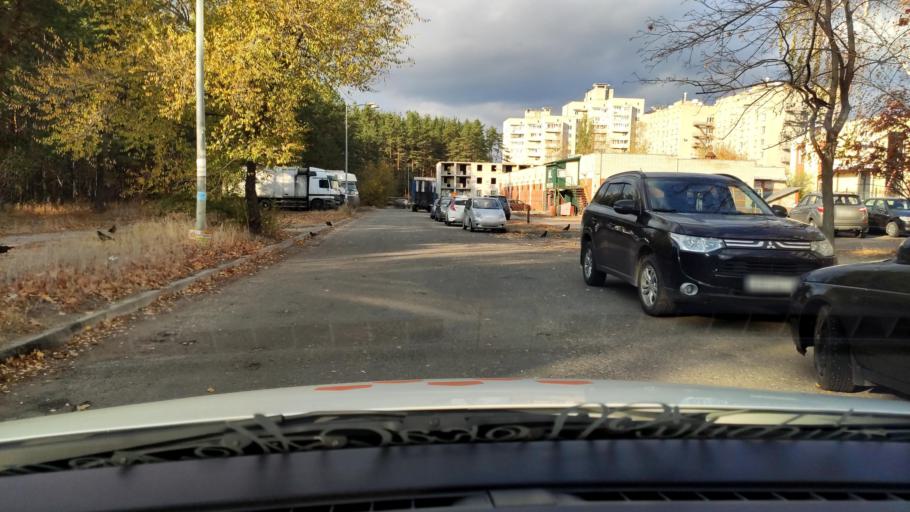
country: RU
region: Voronezj
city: Podgornoye
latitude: 51.7248
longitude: 39.1757
